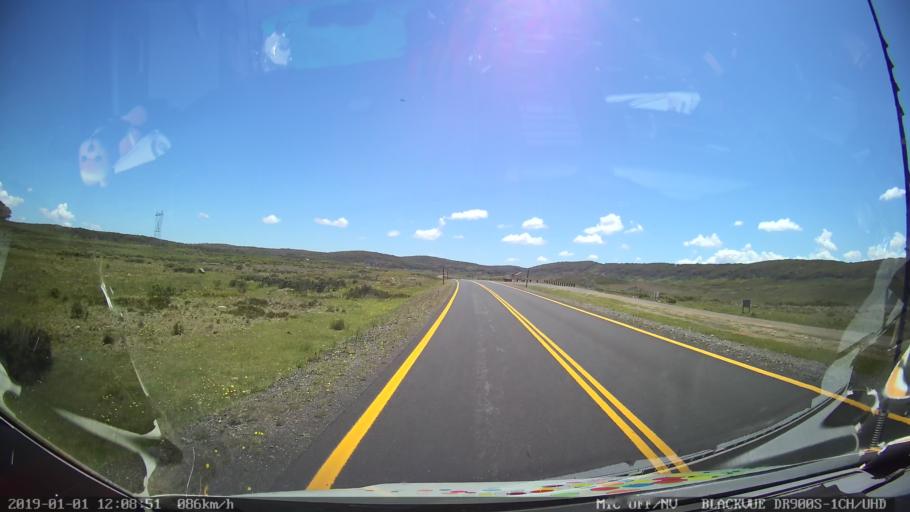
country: AU
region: New South Wales
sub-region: Tumut Shire
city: Tumut
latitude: -35.8150
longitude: 148.4961
